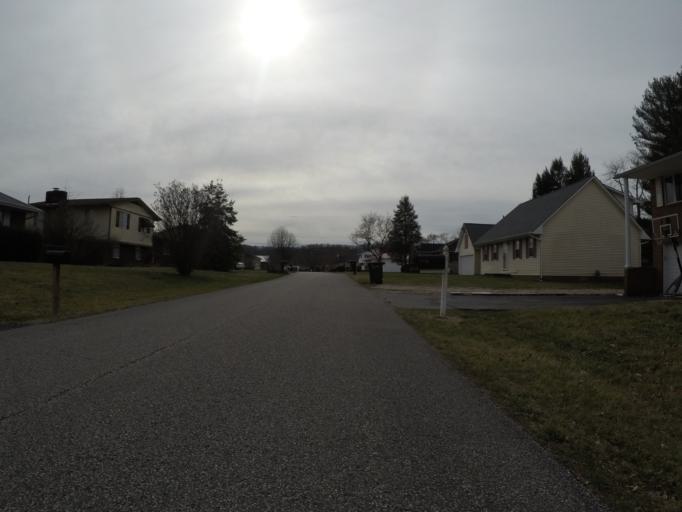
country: US
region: West Virginia
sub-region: Cabell County
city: Pea Ridge
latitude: 38.4499
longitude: -82.3390
